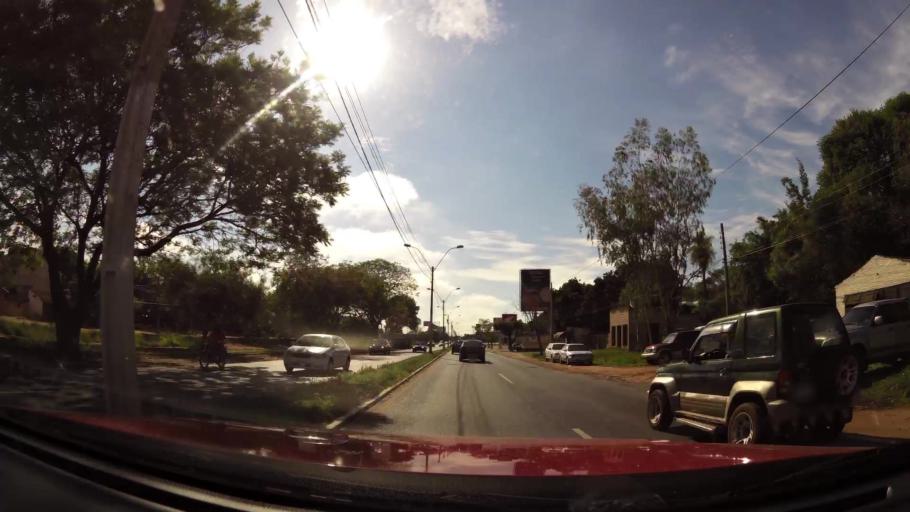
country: PY
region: Central
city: Fernando de la Mora
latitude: -25.2641
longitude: -57.5092
